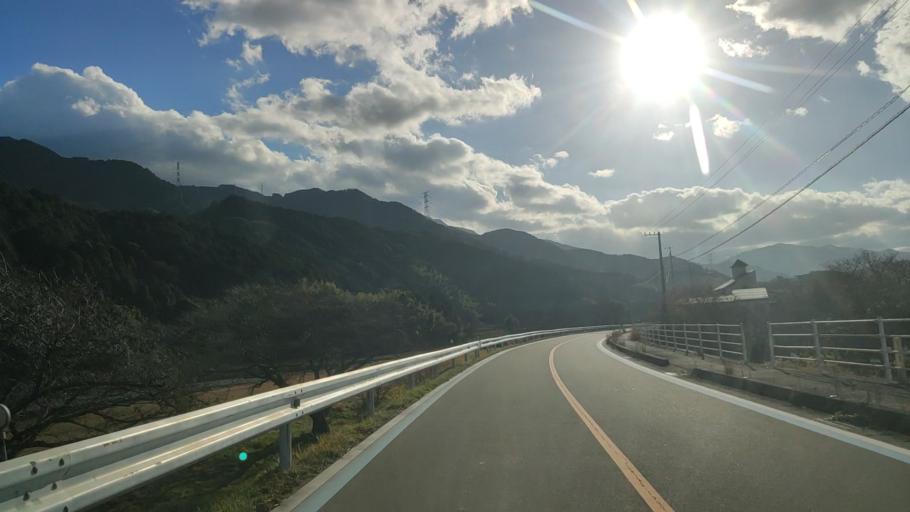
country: JP
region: Ehime
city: Saijo
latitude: 33.8931
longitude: 133.1942
